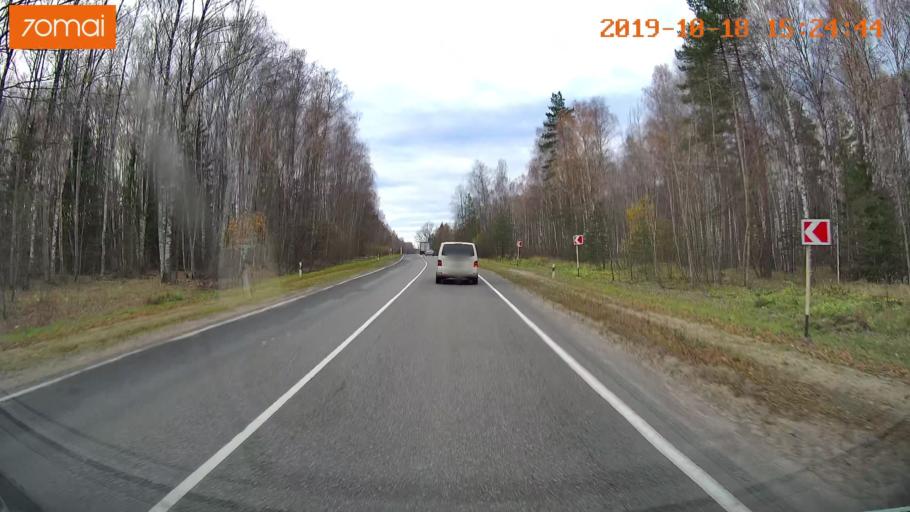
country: RU
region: Vladimir
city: Anopino
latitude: 55.7368
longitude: 40.7187
